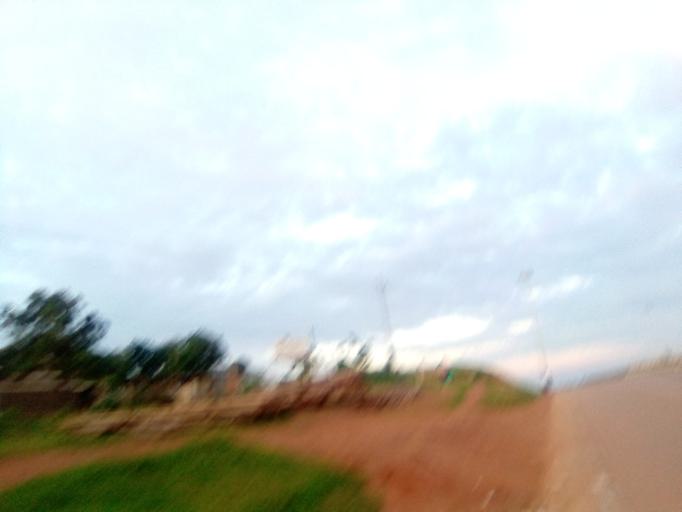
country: UG
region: Central Region
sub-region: Wakiso District
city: Entebbe
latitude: 0.1046
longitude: 32.5110
